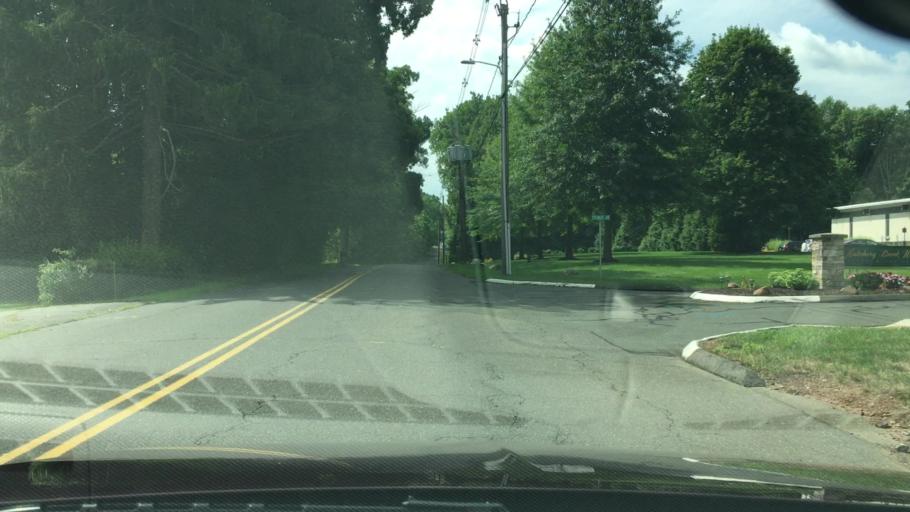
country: US
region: Connecticut
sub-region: Hartford County
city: Kensington
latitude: 41.6219
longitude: -72.7665
